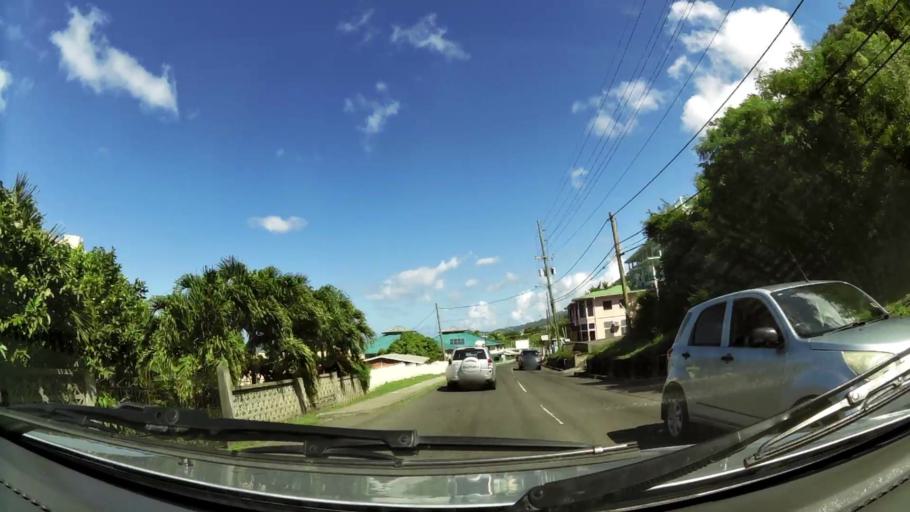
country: GD
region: Saint George
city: Saint George's
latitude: 12.0203
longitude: -61.7595
